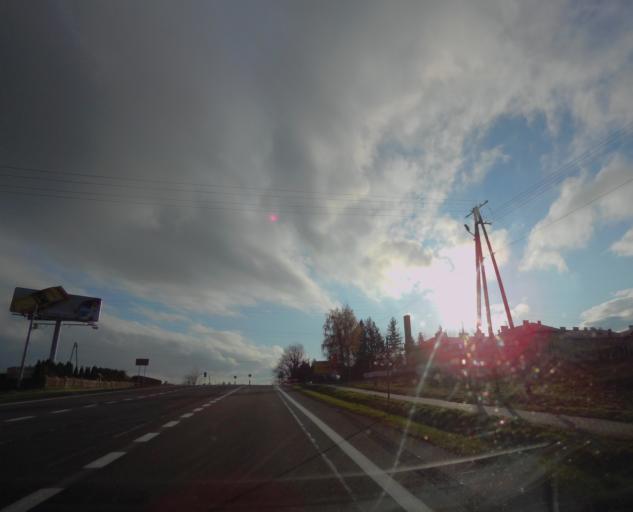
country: PL
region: Subcarpathian Voivodeship
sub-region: Powiat przemyski
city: Orly
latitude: 49.8701
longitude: 22.8105
